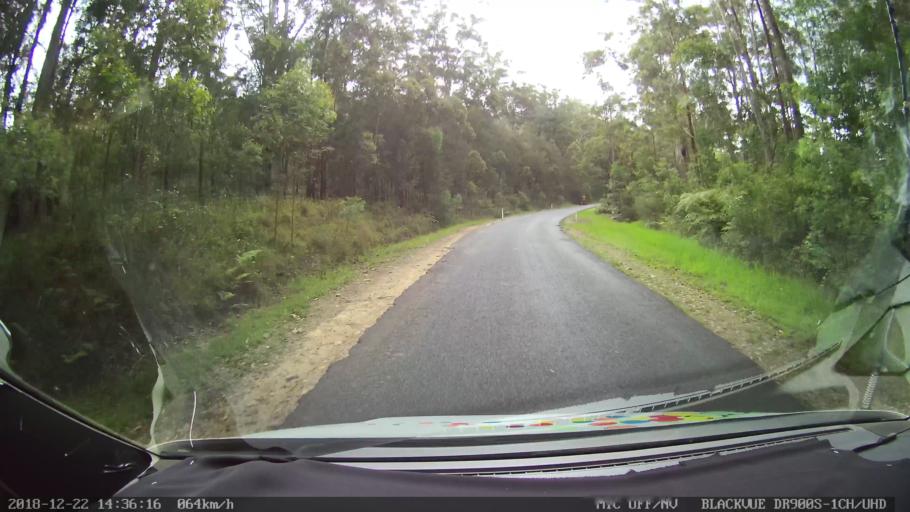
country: AU
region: New South Wales
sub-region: Bellingen
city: Dorrigo
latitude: -30.1279
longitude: 152.6079
